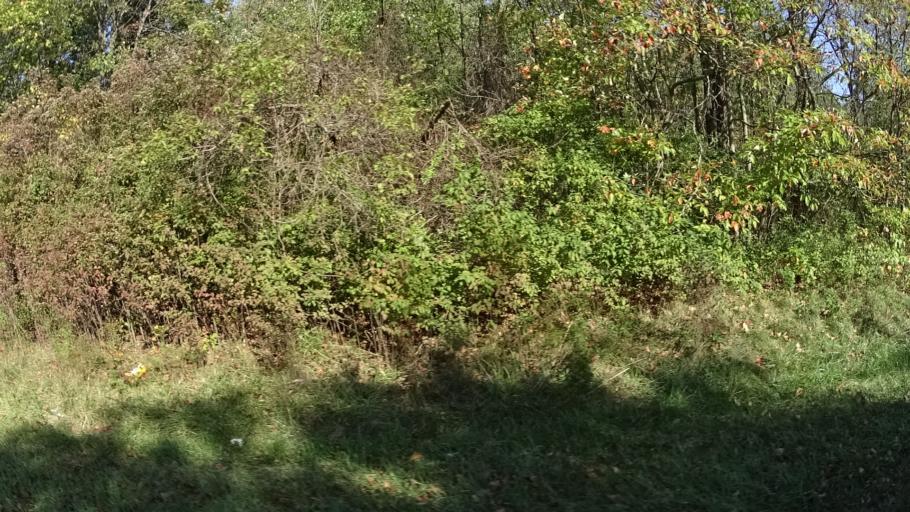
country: US
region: Ohio
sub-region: Lorain County
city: Vermilion-on-the-Lake
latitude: 41.4095
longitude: -82.3346
